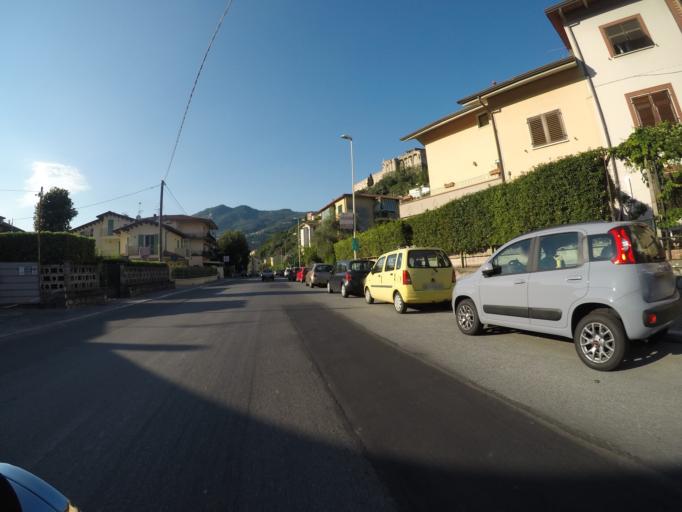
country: IT
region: Tuscany
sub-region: Provincia di Massa-Carrara
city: Massa
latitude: 44.0298
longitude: 10.1443
